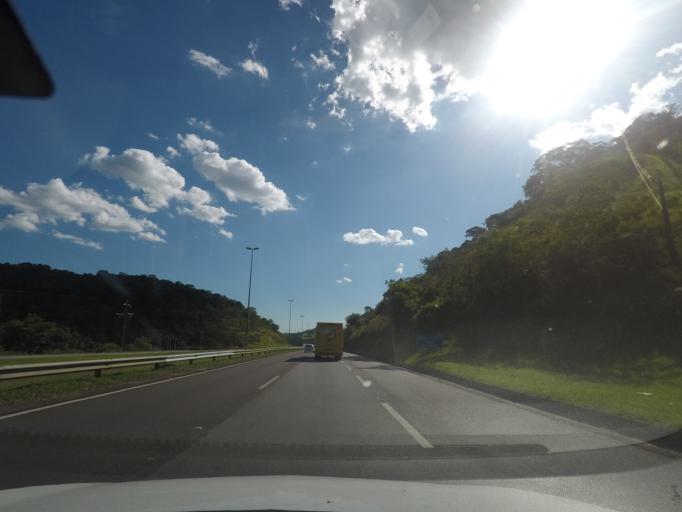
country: BR
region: Rio de Janeiro
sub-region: Guapimirim
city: Guapimirim
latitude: -22.5813
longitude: -43.0129
